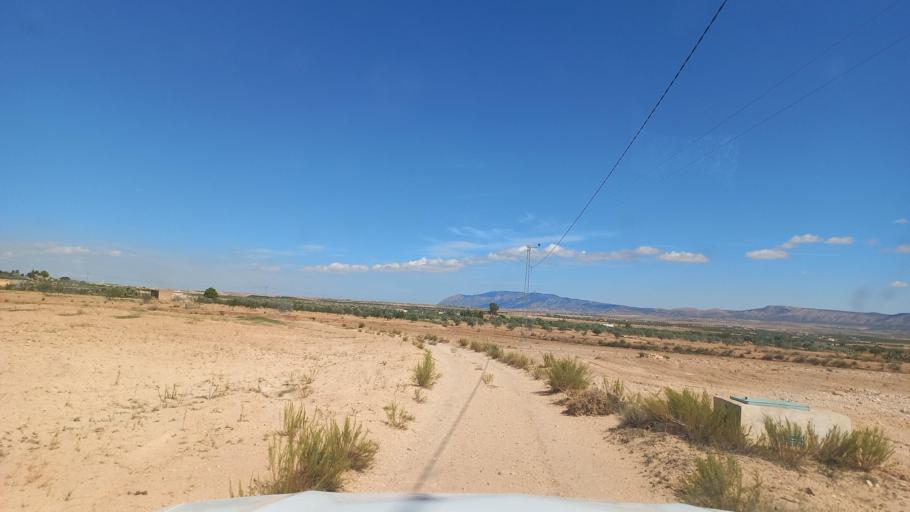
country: TN
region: Al Qasrayn
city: Sbiba
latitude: 35.3551
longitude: 9.0140
